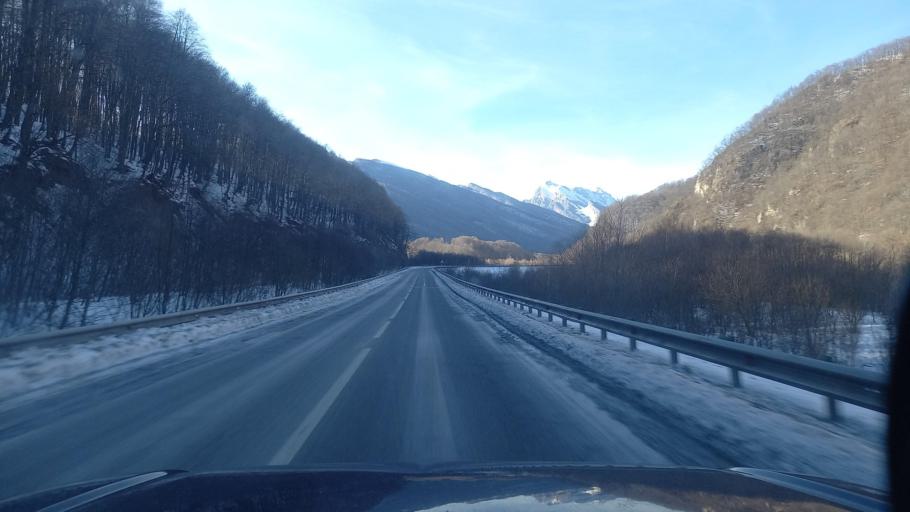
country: RU
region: North Ossetia
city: Gizel'
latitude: 42.9332
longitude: 44.5515
